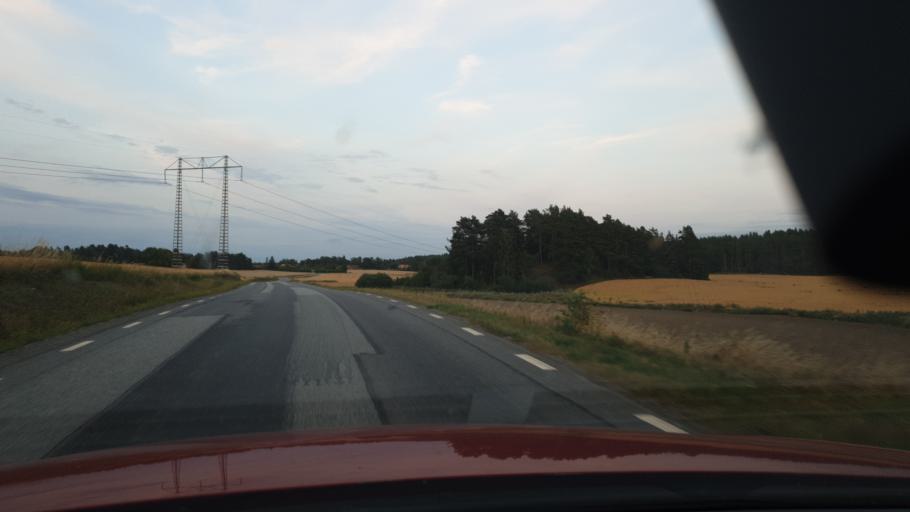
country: SE
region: Uppsala
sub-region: Enkopings Kommun
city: Orsundsbro
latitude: 59.6752
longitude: 17.4211
